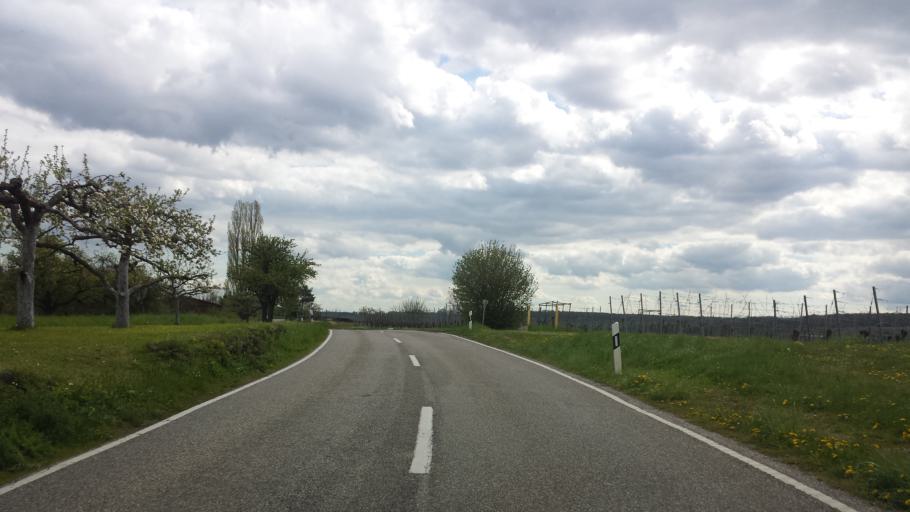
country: DE
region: Baden-Wuerttemberg
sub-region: Regierungsbezirk Stuttgart
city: Vaihingen an der Enz
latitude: 48.9133
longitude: 8.9606
